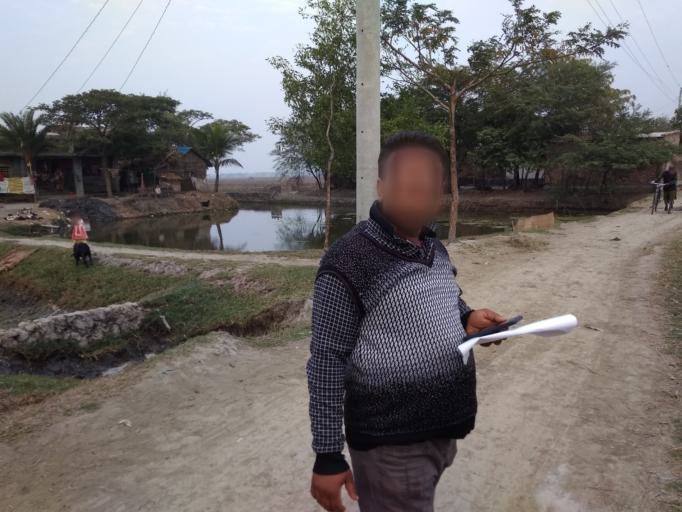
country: BD
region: Khulna
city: Satkhira
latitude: 22.5982
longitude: 89.0464
